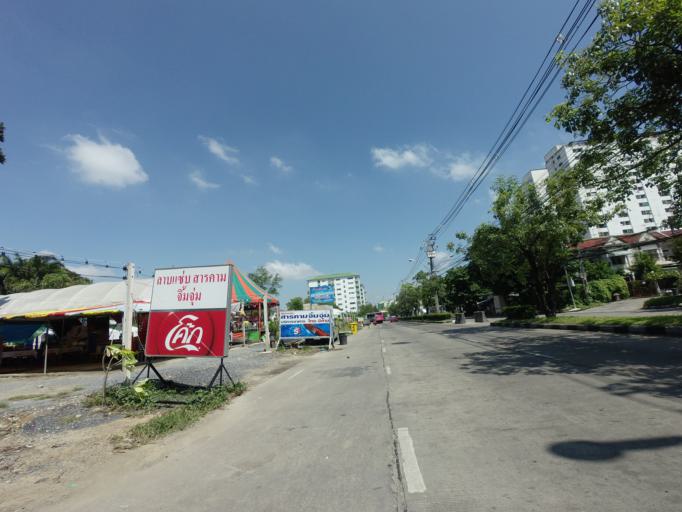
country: TH
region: Bangkok
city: Bang Kapi
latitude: 13.7751
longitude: 100.6412
